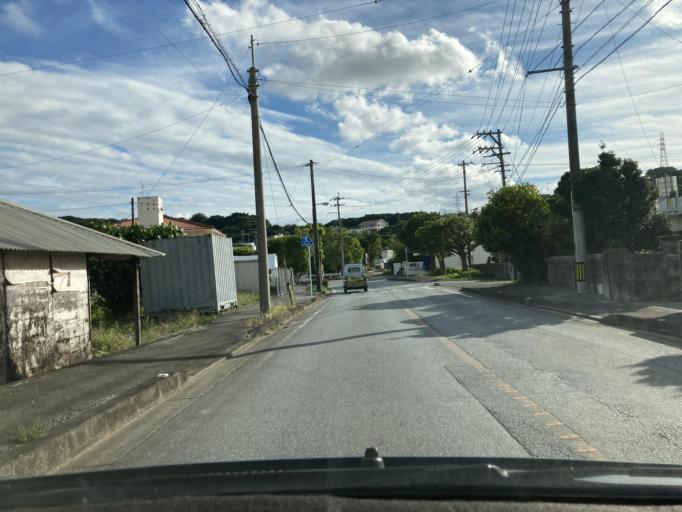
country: JP
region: Okinawa
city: Itoman
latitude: 26.1353
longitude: 127.6986
